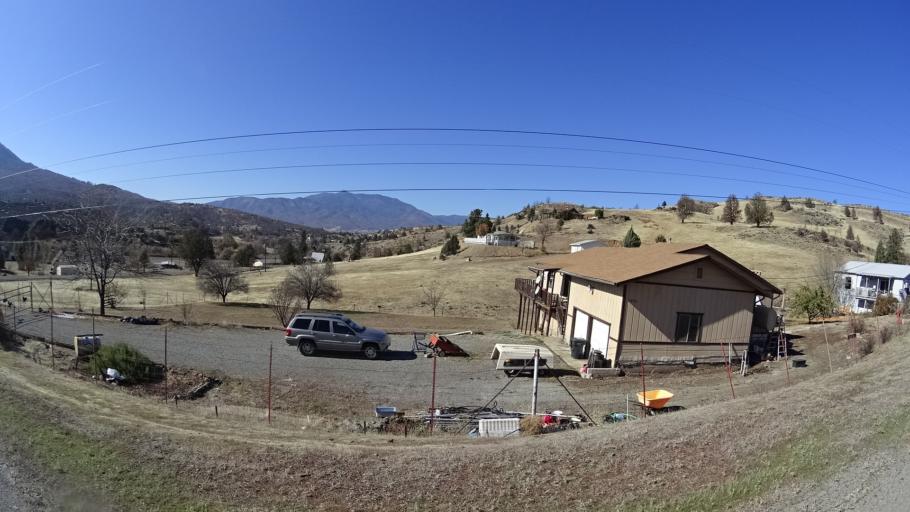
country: US
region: California
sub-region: Siskiyou County
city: Montague
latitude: 41.9006
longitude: -122.4852
